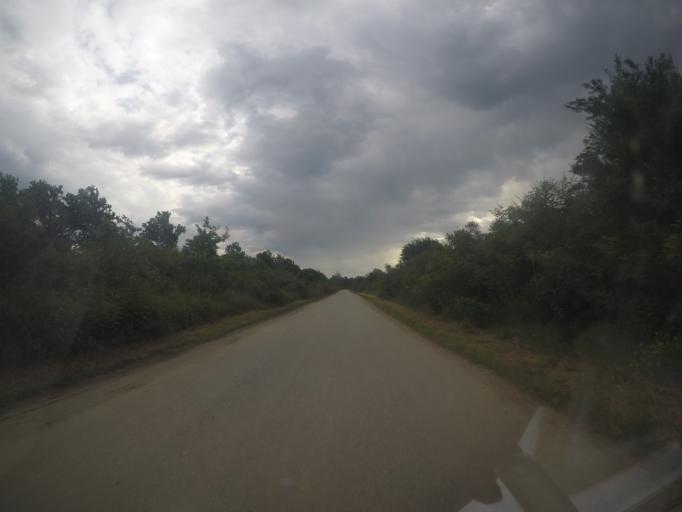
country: RS
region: Central Serbia
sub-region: Belgrade
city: Zemun
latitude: 44.8969
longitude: 20.3999
